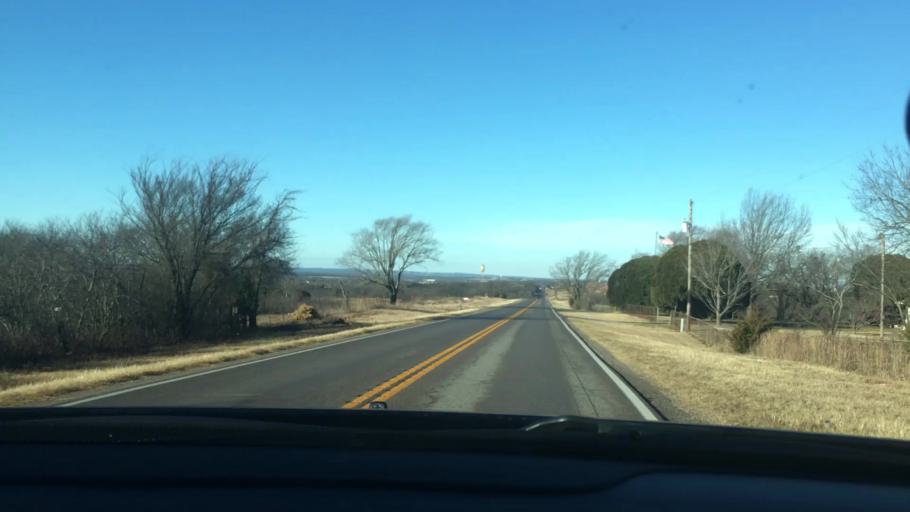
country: US
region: Oklahoma
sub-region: Murray County
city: Sulphur
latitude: 34.5109
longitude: -96.9341
